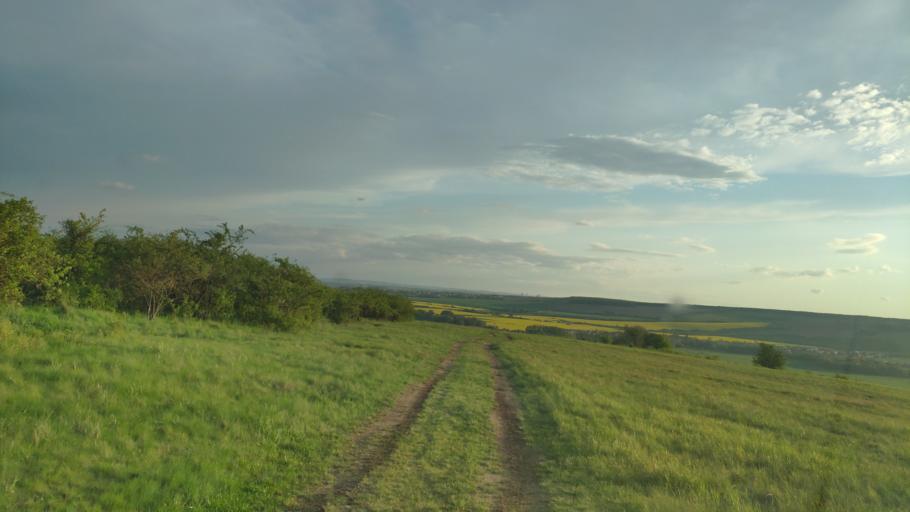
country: SK
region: Kosicky
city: Kosice
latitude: 48.7172
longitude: 21.3565
